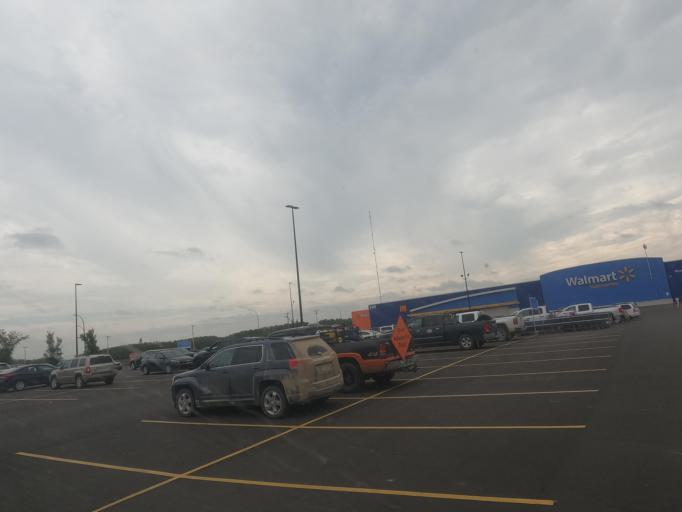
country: CA
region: Saskatchewan
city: Yorkton
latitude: 51.2061
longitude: -102.4457
